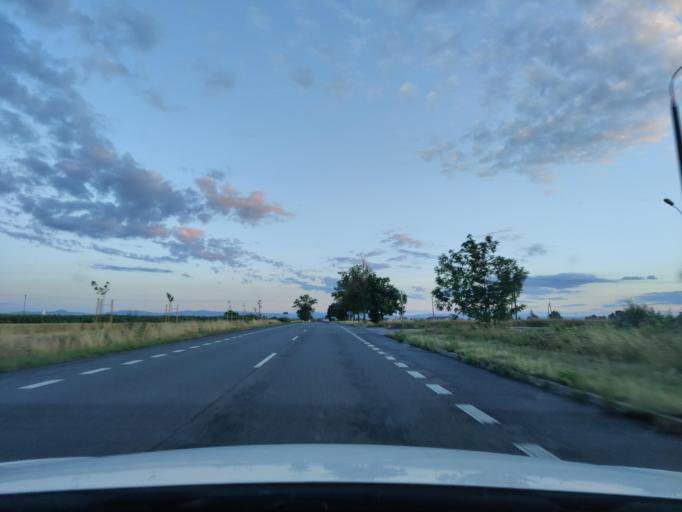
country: PL
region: Opole Voivodeship
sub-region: Powiat nyski
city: Pakoslawice
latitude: 50.5522
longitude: 17.3761
